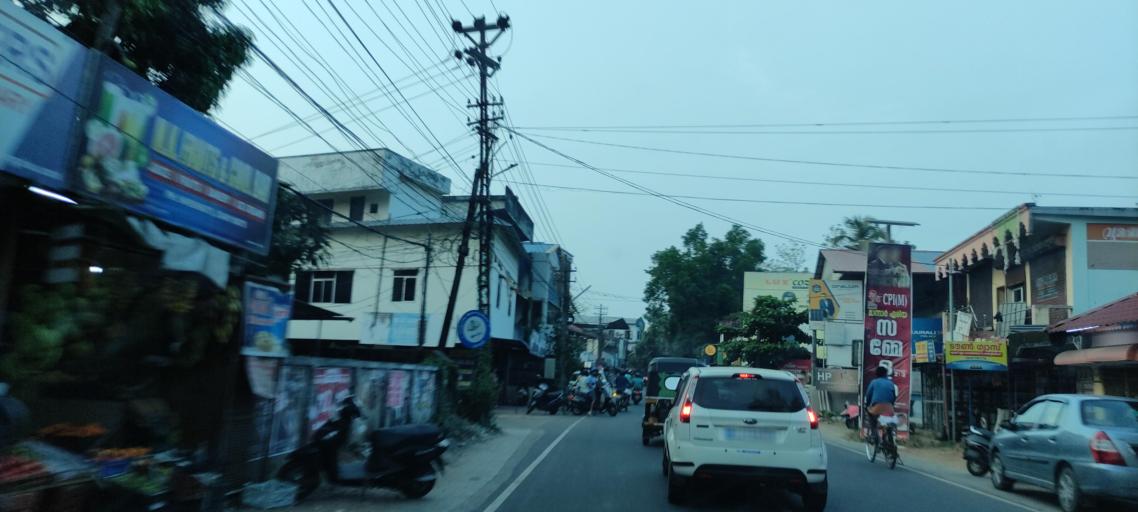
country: IN
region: Kerala
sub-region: Alappuzha
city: Mavelikara
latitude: 9.3126
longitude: 76.5340
